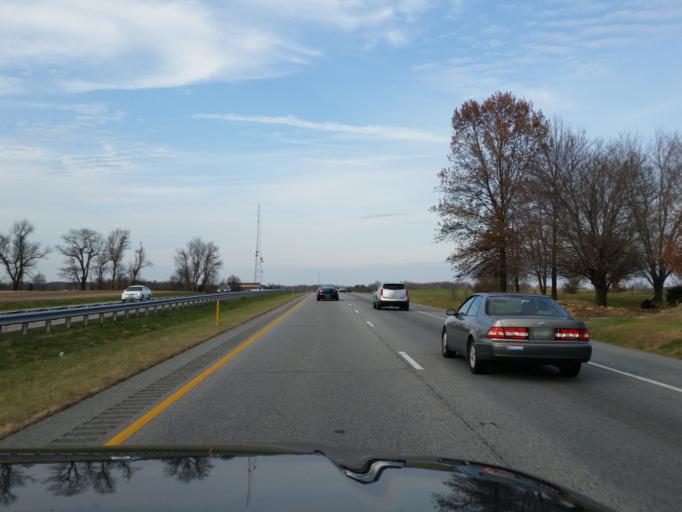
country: US
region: Maryland
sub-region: Queen Anne's County
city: Centreville
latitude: 38.9280
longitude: -76.0622
